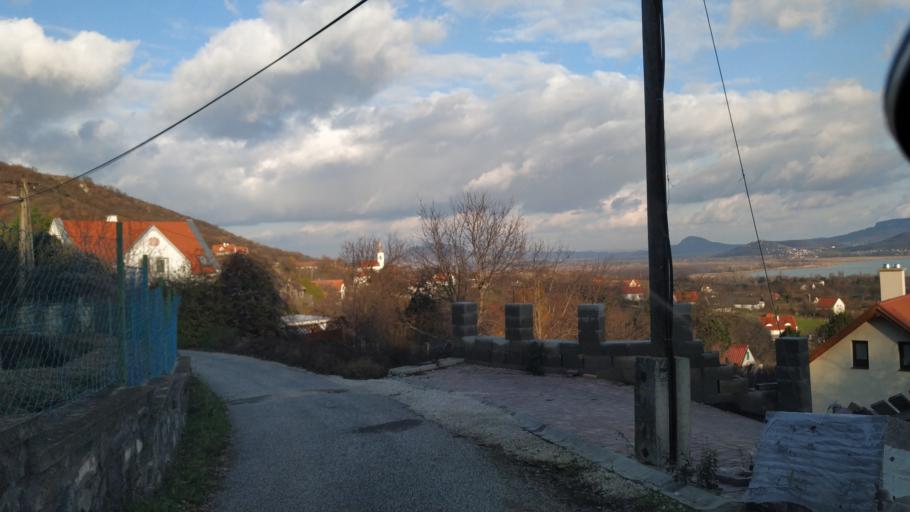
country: HU
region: Zala
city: Vonyarcvashegy
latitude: 46.7853
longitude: 17.3616
